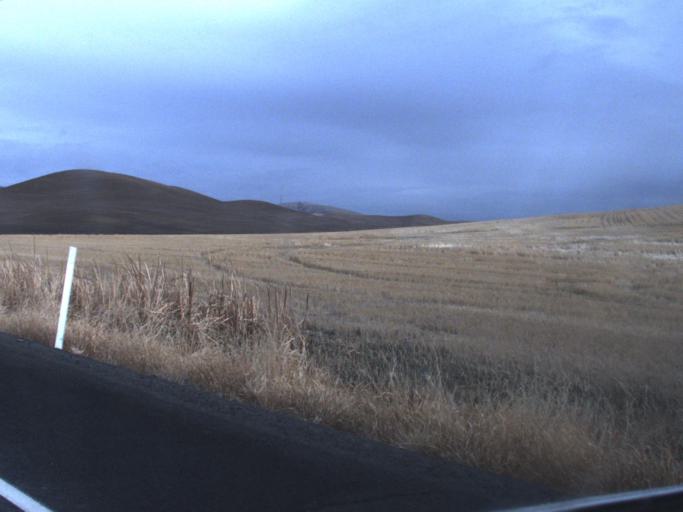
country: US
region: Washington
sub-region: Whitman County
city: Pullman
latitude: 46.6045
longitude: -117.1651
